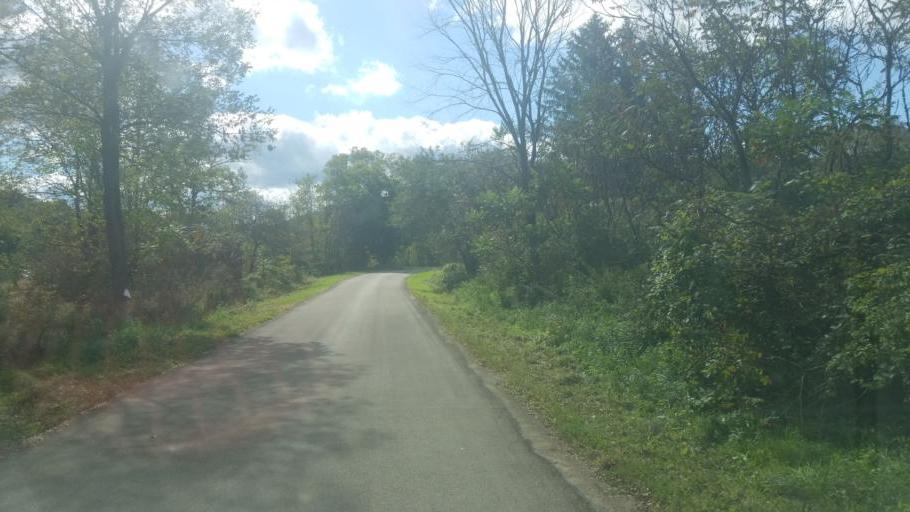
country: US
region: New York
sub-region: Cattaraugus County
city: Franklinville
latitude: 42.2407
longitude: -78.3989
